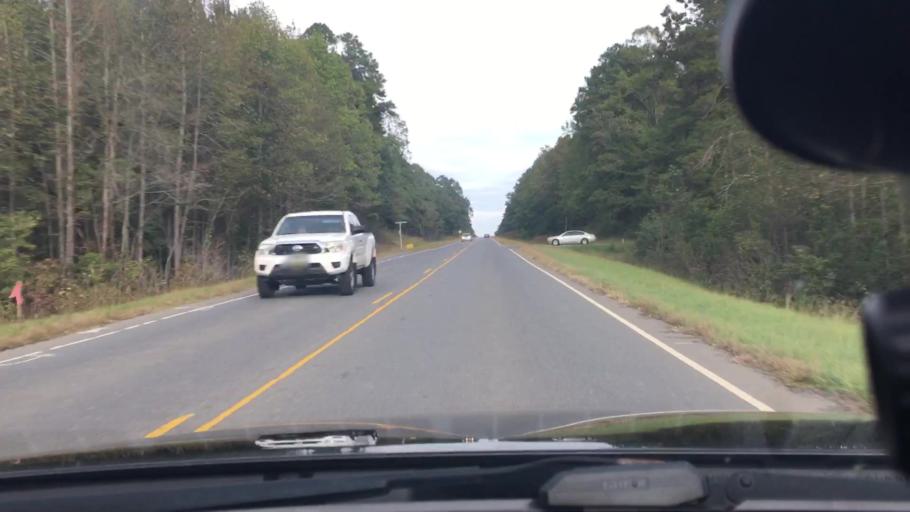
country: US
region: North Carolina
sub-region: Montgomery County
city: Troy
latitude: 35.3166
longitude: -79.9768
